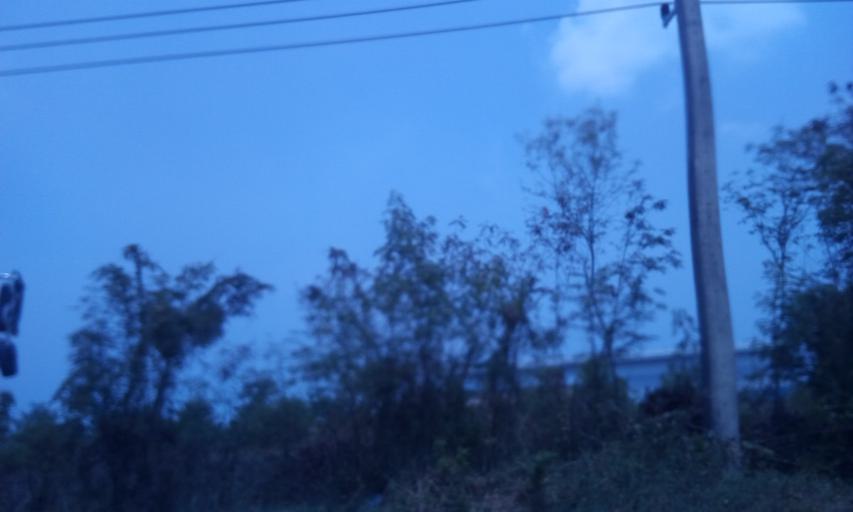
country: TH
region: Bangkok
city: Nong Chok
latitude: 13.9639
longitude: 100.9118
